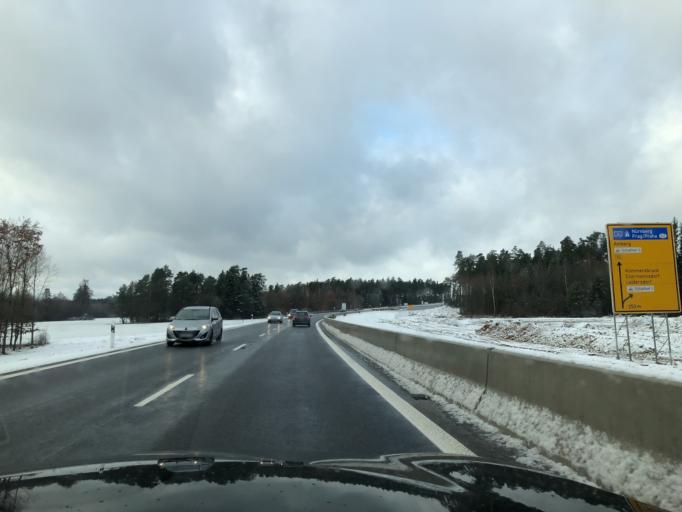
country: DE
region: Bavaria
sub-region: Upper Palatinate
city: Breitenbrunn
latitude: 49.3904
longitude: 11.9907
